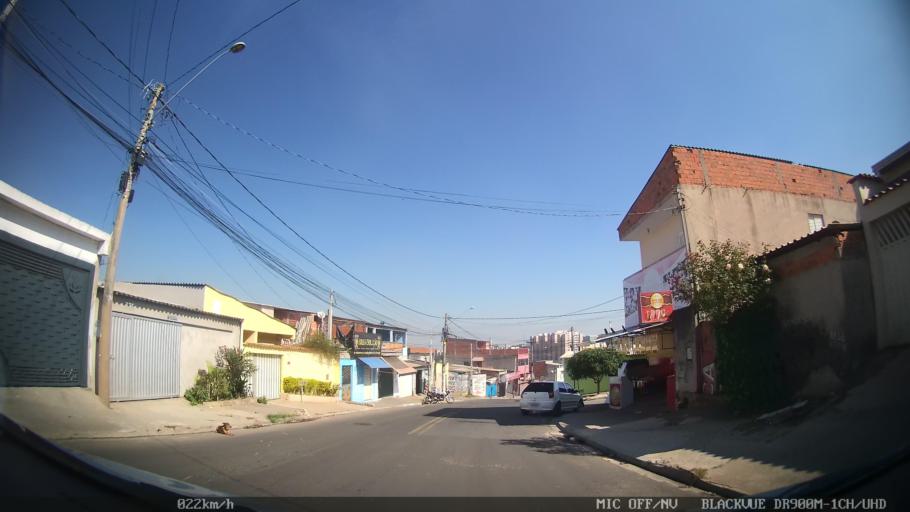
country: BR
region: Sao Paulo
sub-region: Campinas
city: Campinas
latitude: -22.9446
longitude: -47.0825
